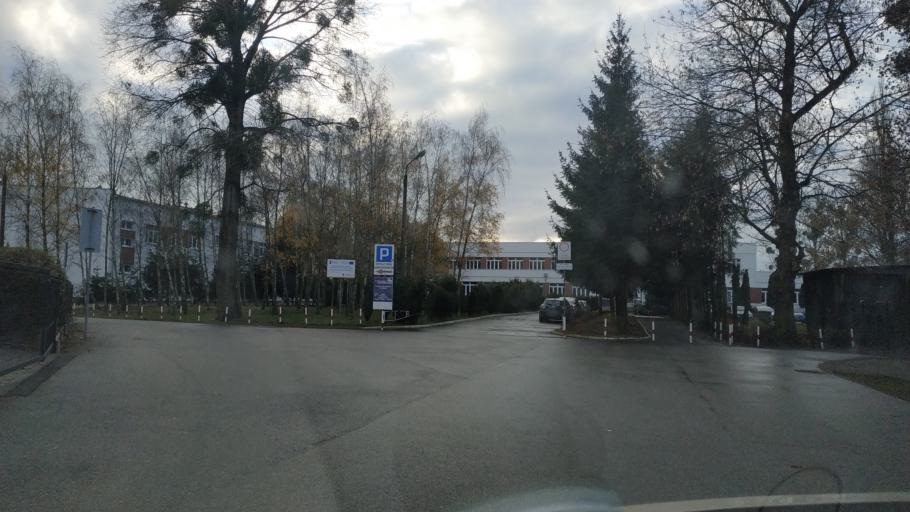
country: PL
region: Kujawsko-Pomorskie
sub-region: Torun
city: Torun
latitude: 53.0230
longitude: 18.5885
